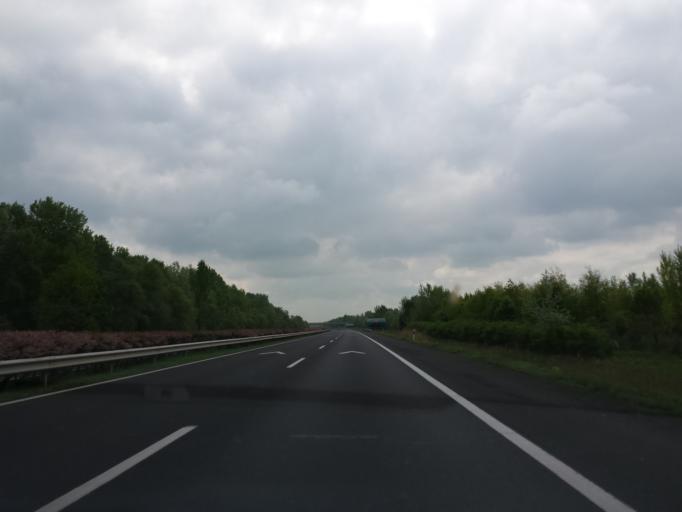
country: HU
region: Gyor-Moson-Sopron
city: Mosonmagyarovar
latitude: 47.8124
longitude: 17.2947
